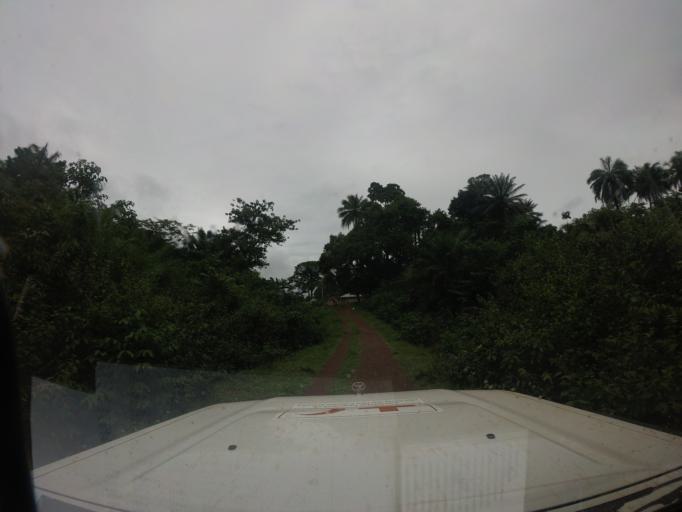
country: SL
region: Northern Province
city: Kambia
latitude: 9.1807
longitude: -12.8907
